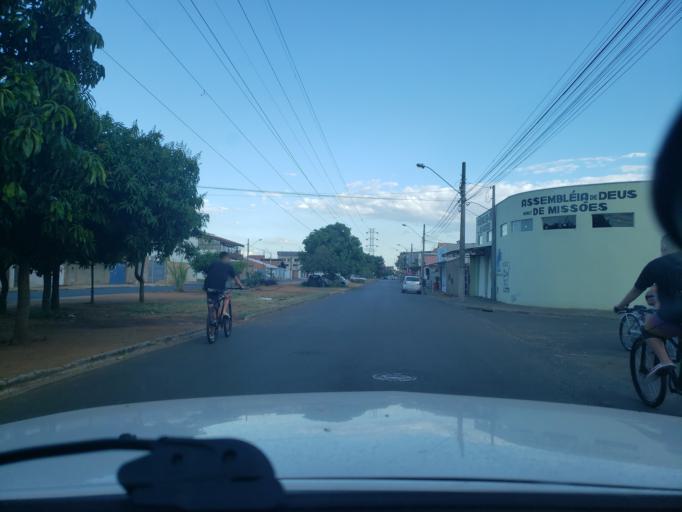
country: BR
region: Sao Paulo
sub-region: Moji-Guacu
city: Mogi-Gaucu
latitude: -22.3249
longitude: -46.9216
